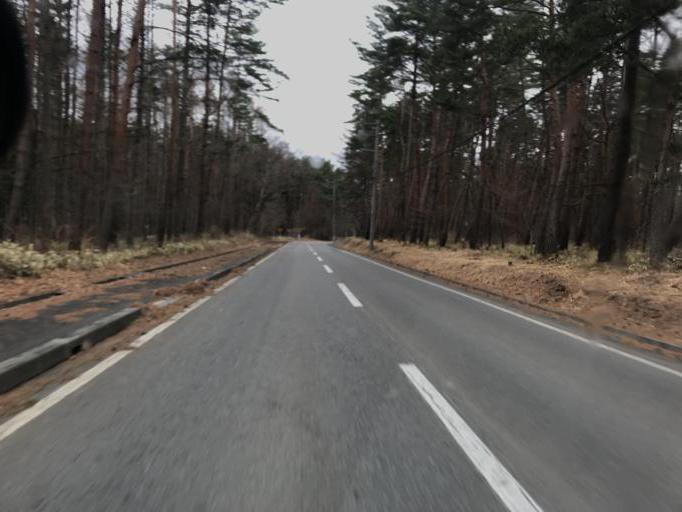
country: JP
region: Nagano
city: Chino
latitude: 35.9238
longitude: 138.2924
